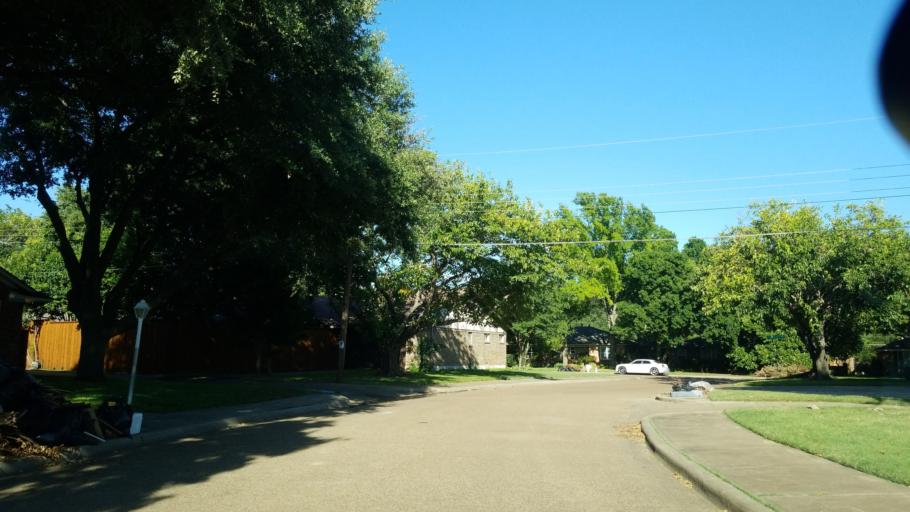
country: US
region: Texas
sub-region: Dallas County
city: Highland Park
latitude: 32.7891
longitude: -96.7084
